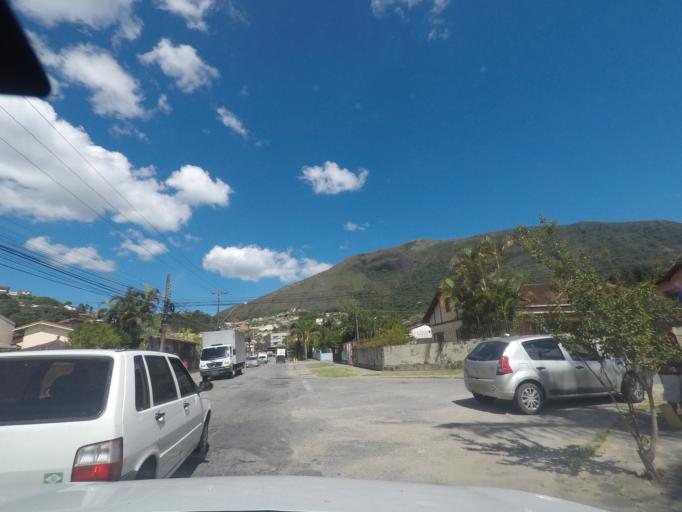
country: BR
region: Rio de Janeiro
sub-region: Teresopolis
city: Teresopolis
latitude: -22.4343
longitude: -42.9737
